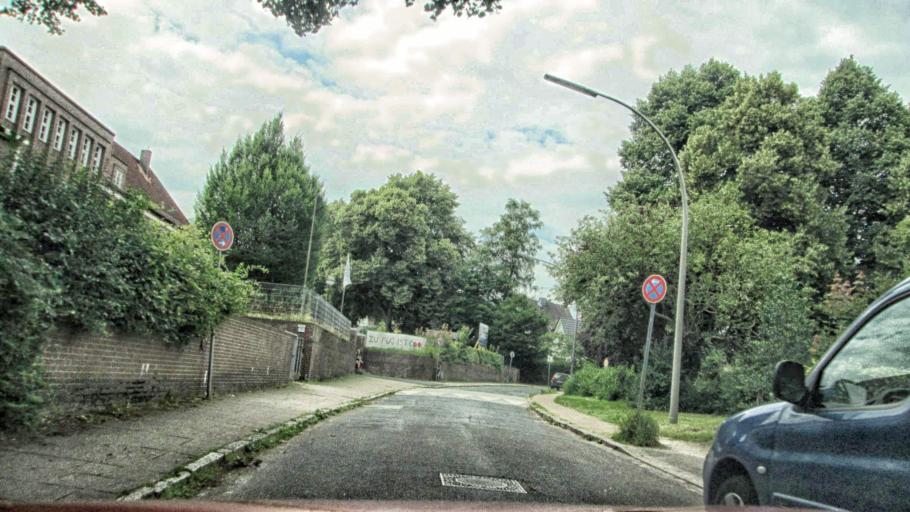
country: DE
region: Schleswig-Holstein
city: Halstenbek
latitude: 53.5643
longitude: 9.8025
